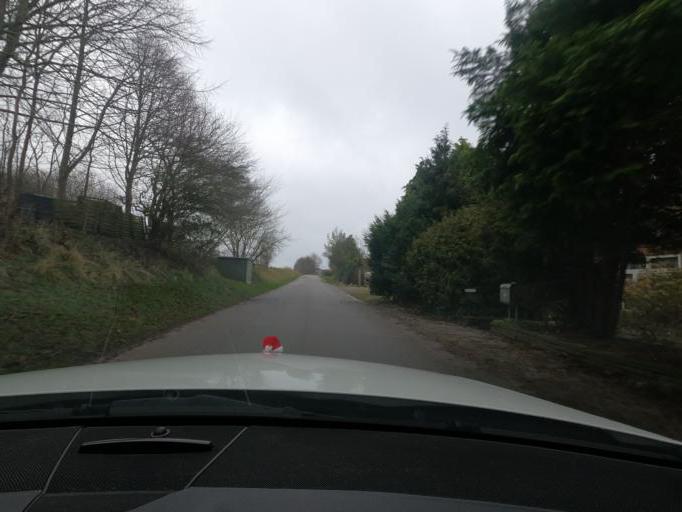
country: DK
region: South Denmark
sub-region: Haderslev Kommune
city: Starup
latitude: 55.2458
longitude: 9.6854
